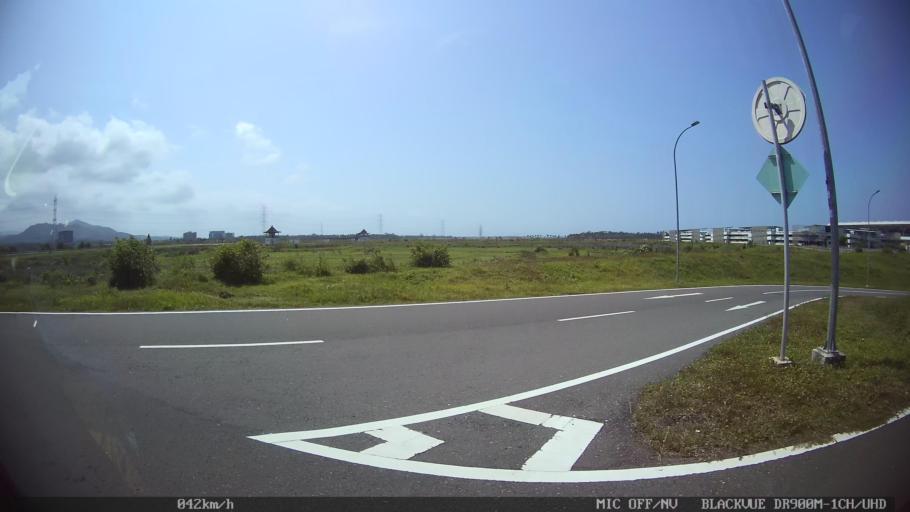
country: ID
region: Daerah Istimewa Yogyakarta
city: Srandakan
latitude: -7.8931
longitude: 110.0582
